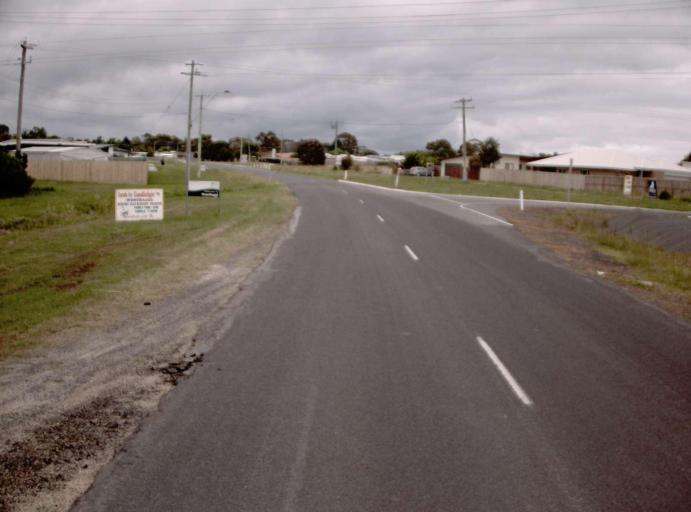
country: AU
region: Victoria
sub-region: Bass Coast
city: North Wonthaggi
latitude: -38.5932
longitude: 145.6098
